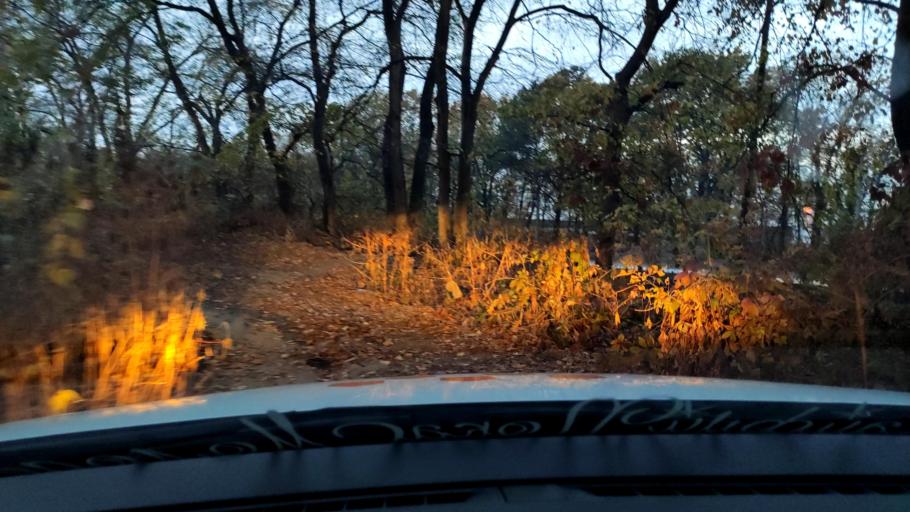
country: RU
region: Voronezj
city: Pridonskoy
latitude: 51.6627
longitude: 39.1178
